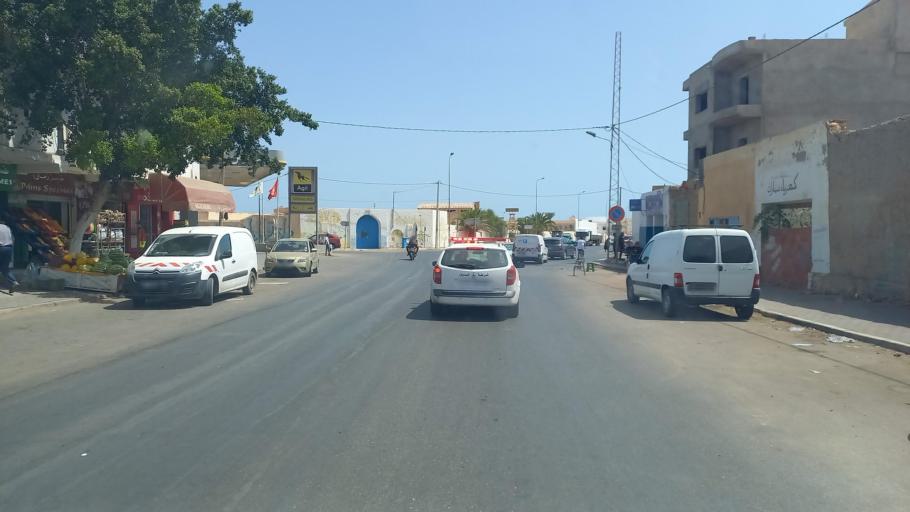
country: TN
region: Madanin
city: Zarzis
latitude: 33.4978
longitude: 11.0918
